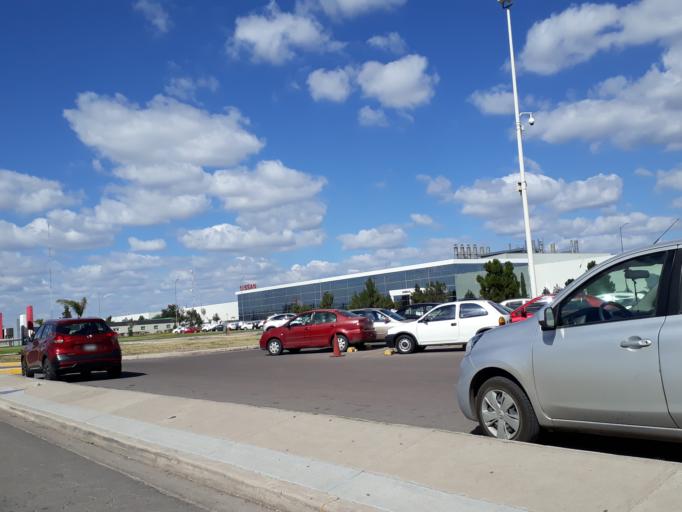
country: MX
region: Aguascalientes
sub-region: Aguascalientes
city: San Sebastian [Fraccionamiento]
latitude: 21.8088
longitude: -102.2843
